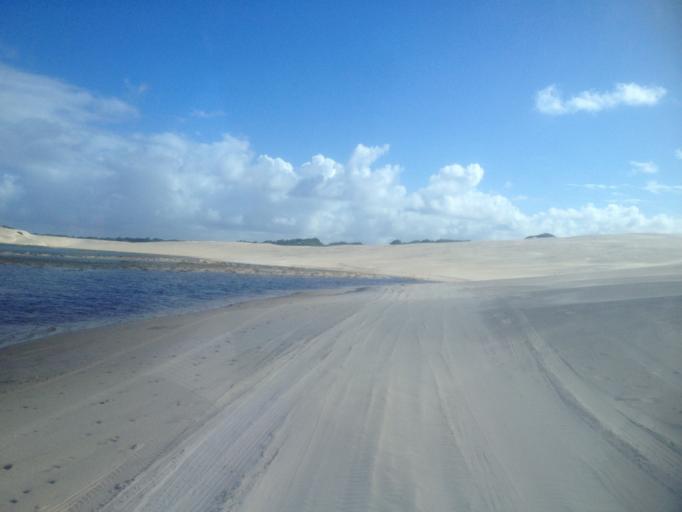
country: BR
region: Sergipe
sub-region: Indiaroba
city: Indiaroba
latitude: -11.4754
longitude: -37.3736
